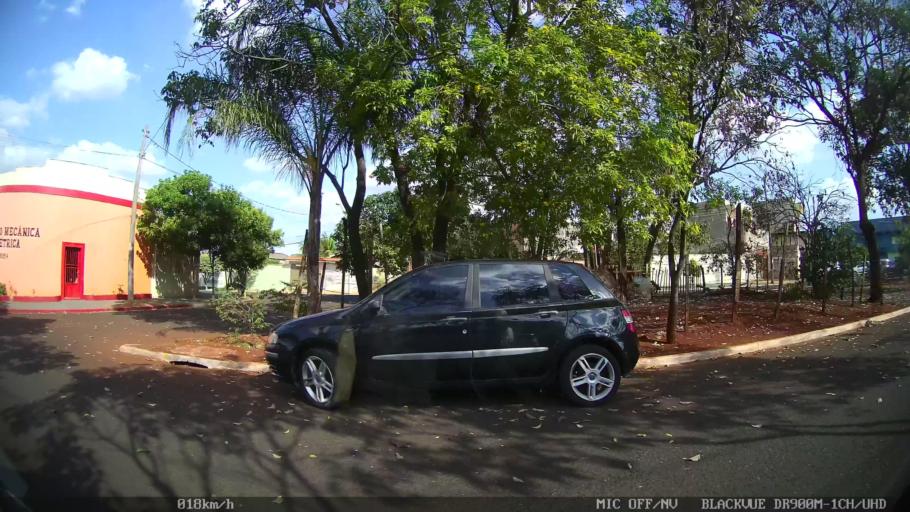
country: BR
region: Sao Paulo
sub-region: Ribeirao Preto
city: Ribeirao Preto
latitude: -21.1963
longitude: -47.8385
